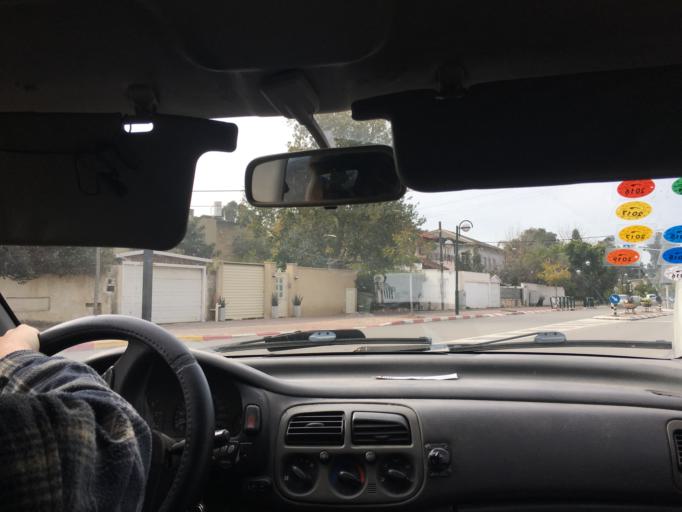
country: IL
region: Tel Aviv
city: Ramat HaSharon
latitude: 32.1357
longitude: 34.8503
